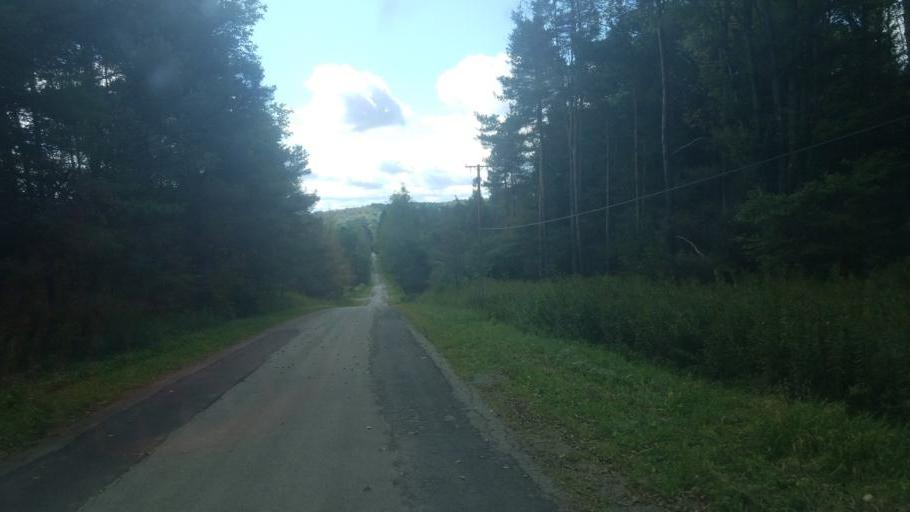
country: US
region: New York
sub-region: Cattaraugus County
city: Franklinville
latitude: 42.2185
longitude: -78.4146
